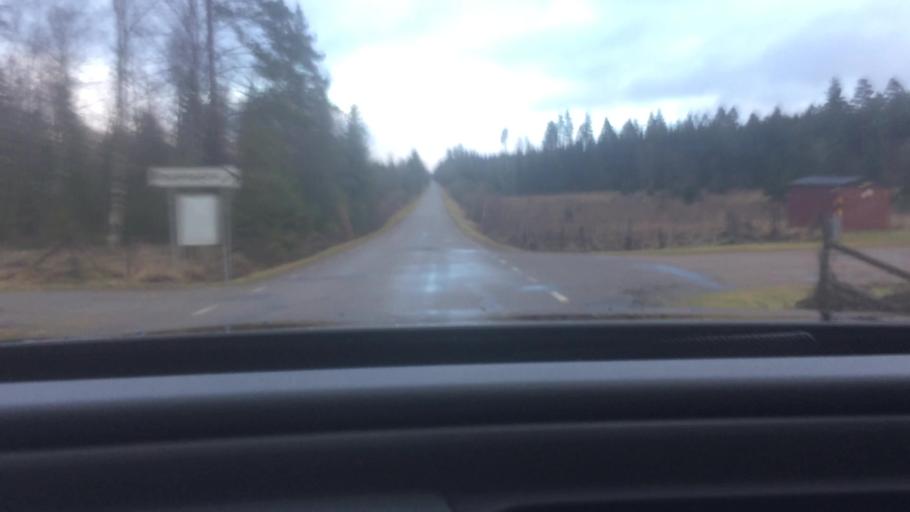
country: SE
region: Vaestra Goetaland
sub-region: Falkopings Kommun
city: Falkoeping
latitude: 57.9987
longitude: 13.4819
